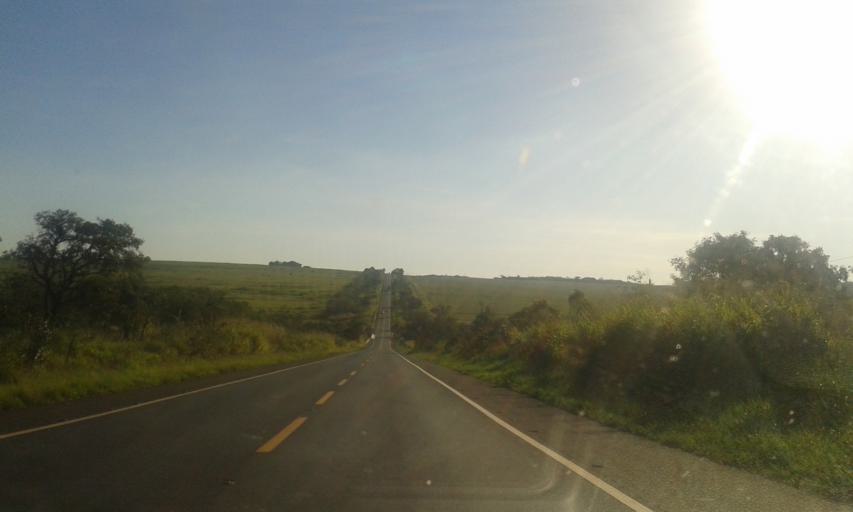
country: BR
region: Minas Gerais
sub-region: Monte Alegre De Minas
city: Monte Alegre de Minas
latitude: -18.8802
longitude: -49.1581
